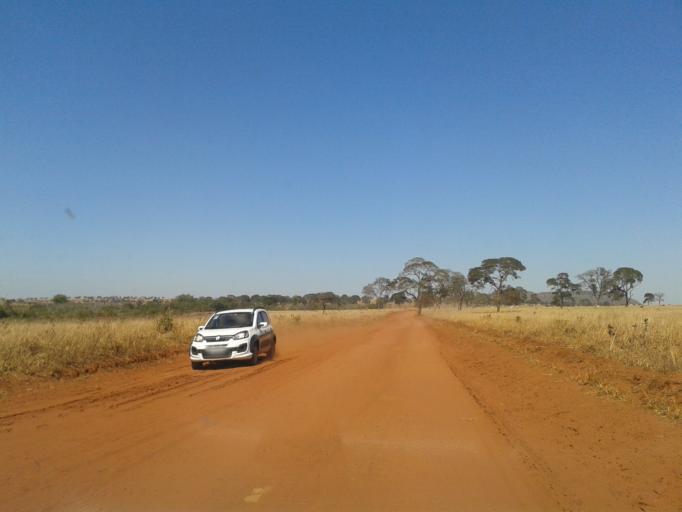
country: BR
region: Minas Gerais
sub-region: Santa Vitoria
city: Santa Vitoria
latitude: -19.1595
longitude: -50.1562
